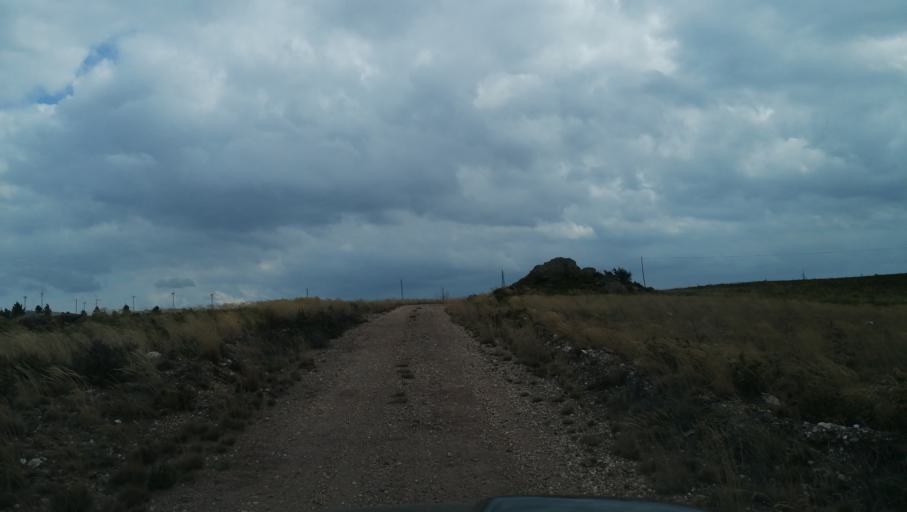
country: PT
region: Vila Real
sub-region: Vila Pouca de Aguiar
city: Vila Pouca de Aguiar
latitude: 41.5329
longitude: -7.7180
